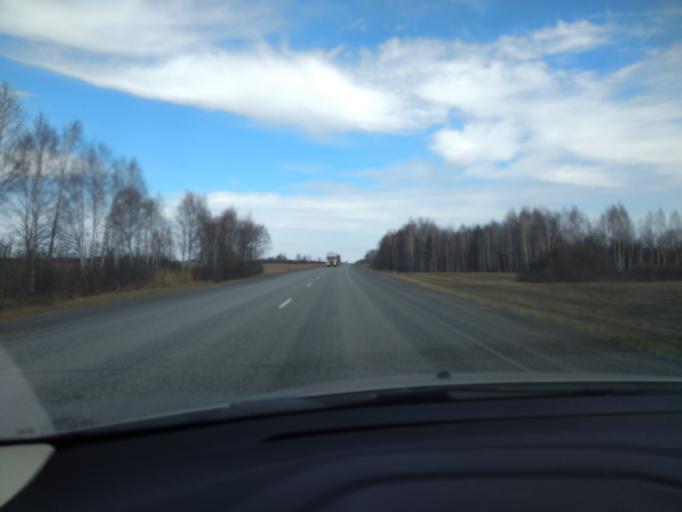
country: RU
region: Sverdlovsk
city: Pyshma
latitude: 56.9968
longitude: 63.2922
